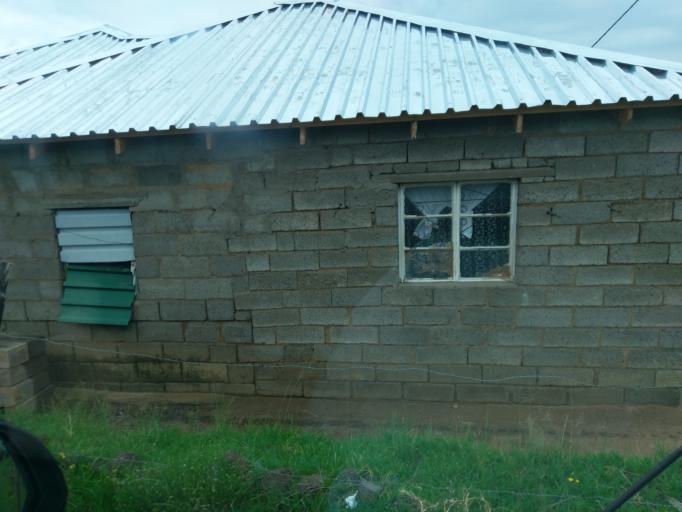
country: LS
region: Berea
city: Teyateyaneng
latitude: -29.1072
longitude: 27.9658
